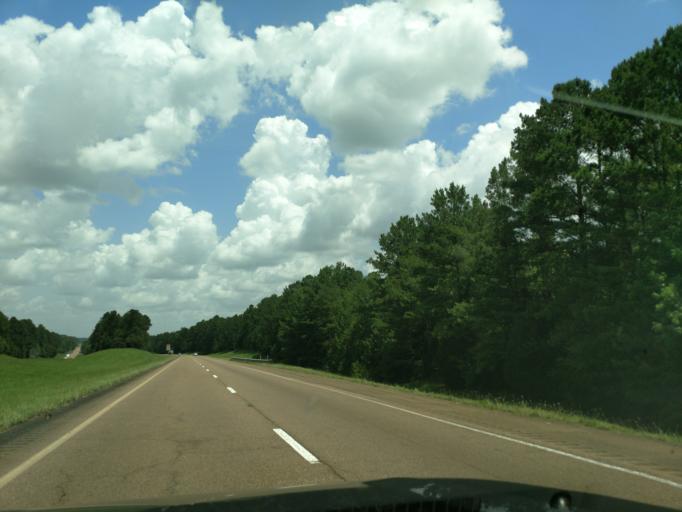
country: US
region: Mississippi
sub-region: Montgomery County
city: Winona
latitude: 33.5046
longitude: -89.7653
